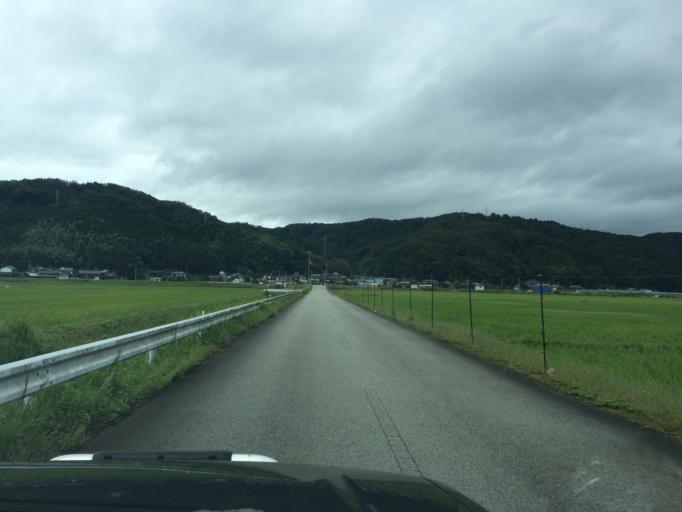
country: JP
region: Hyogo
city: Toyooka
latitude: 35.4904
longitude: 134.7900
